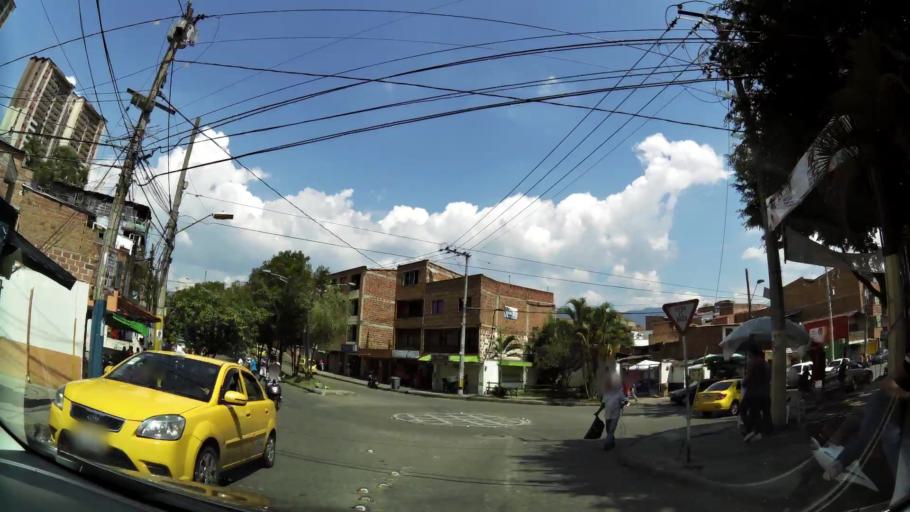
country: CO
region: Antioquia
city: Itagui
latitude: 6.2147
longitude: -75.6021
